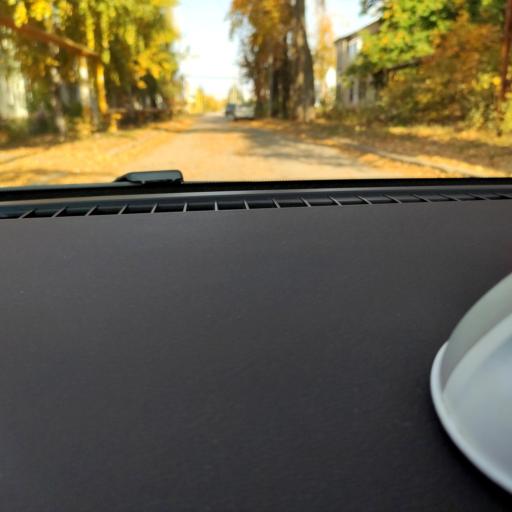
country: RU
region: Samara
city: Samara
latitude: 53.2655
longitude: 50.2392
